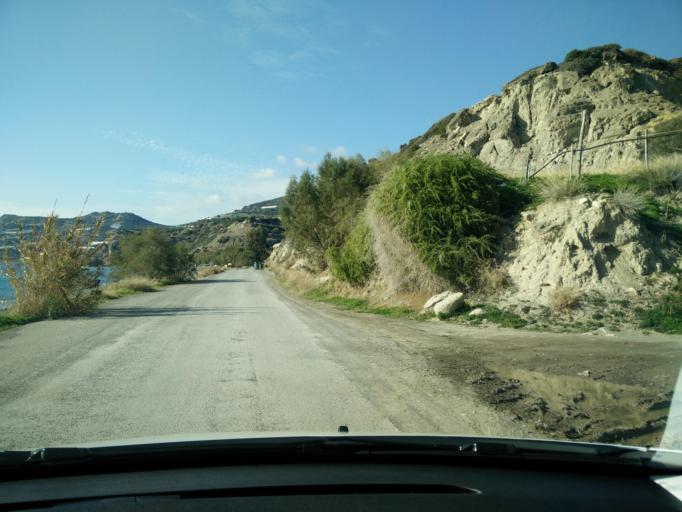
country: GR
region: Crete
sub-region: Nomos Lasithiou
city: Gra Liyia
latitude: 34.9905
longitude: 25.5373
